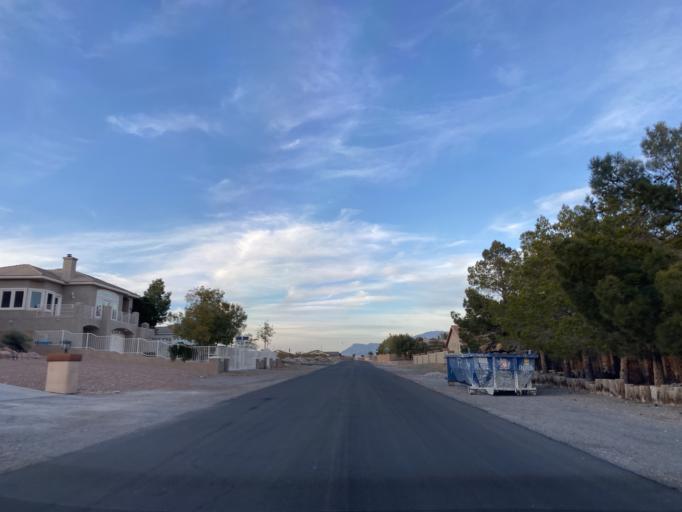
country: US
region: Nevada
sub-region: Clark County
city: Summerlin South
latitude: 36.2893
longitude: -115.3126
